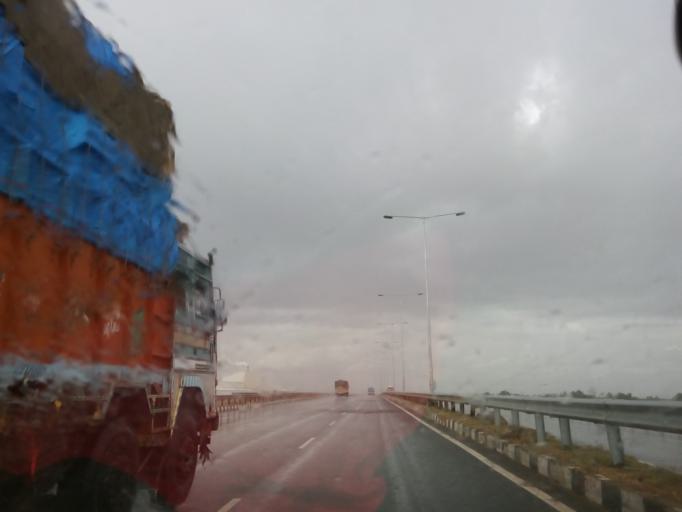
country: IN
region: Karnataka
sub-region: Chitradurga
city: Chitradurga
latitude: 14.1272
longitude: 76.5080
